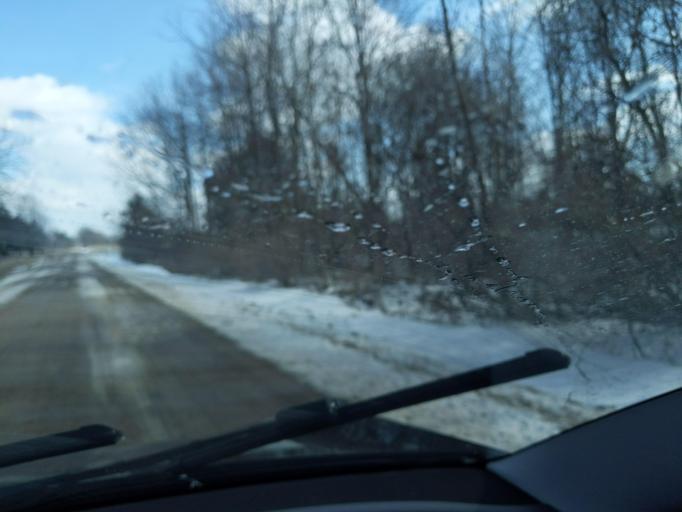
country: US
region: Michigan
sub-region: Ingham County
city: Webberville
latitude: 42.6140
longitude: -84.1317
